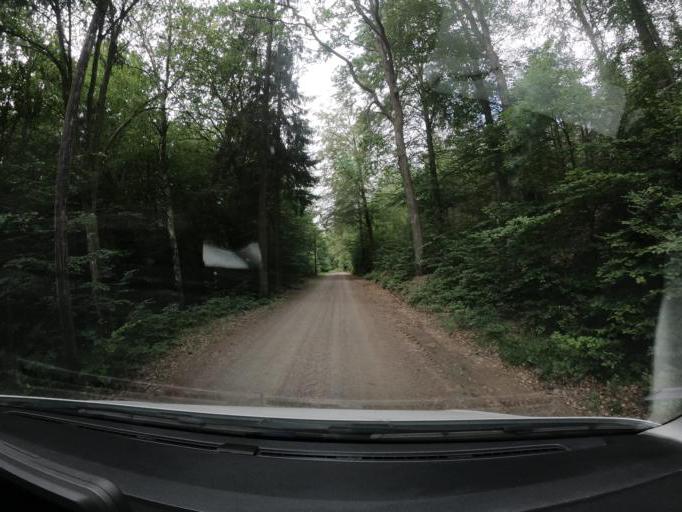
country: SE
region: Skane
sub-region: Hassleholms Kommun
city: Sosdala
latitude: 56.0649
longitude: 13.5681
